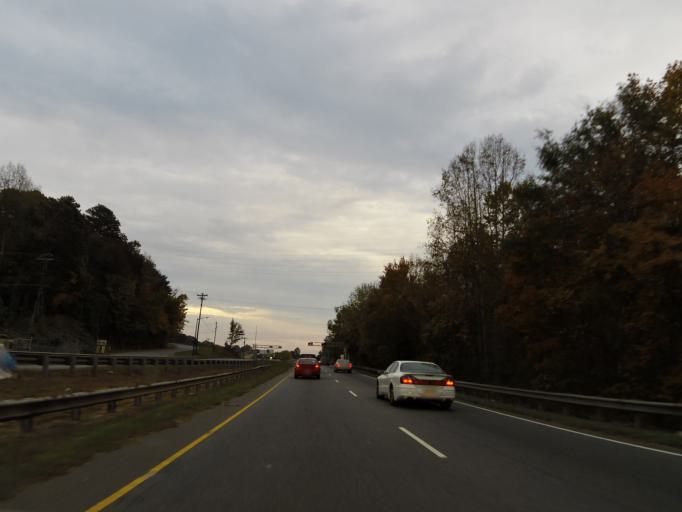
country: US
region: North Carolina
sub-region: Caldwell County
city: Northlakes
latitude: 35.7567
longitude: -81.3760
